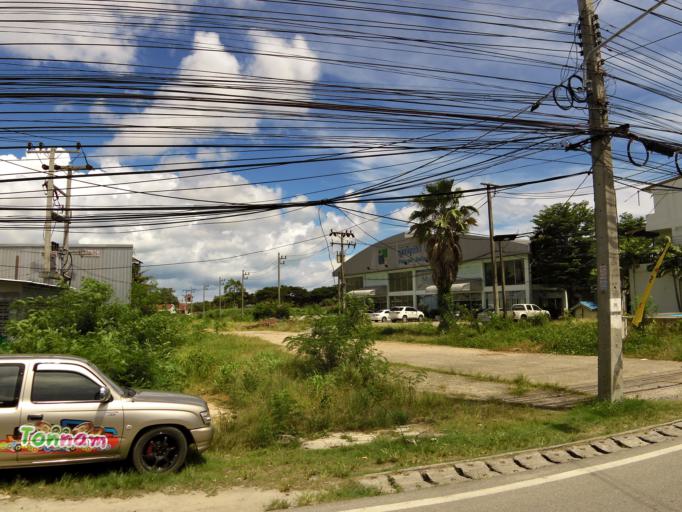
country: TH
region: Phuket
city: Ban Chalong
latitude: 7.8451
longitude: 98.3344
